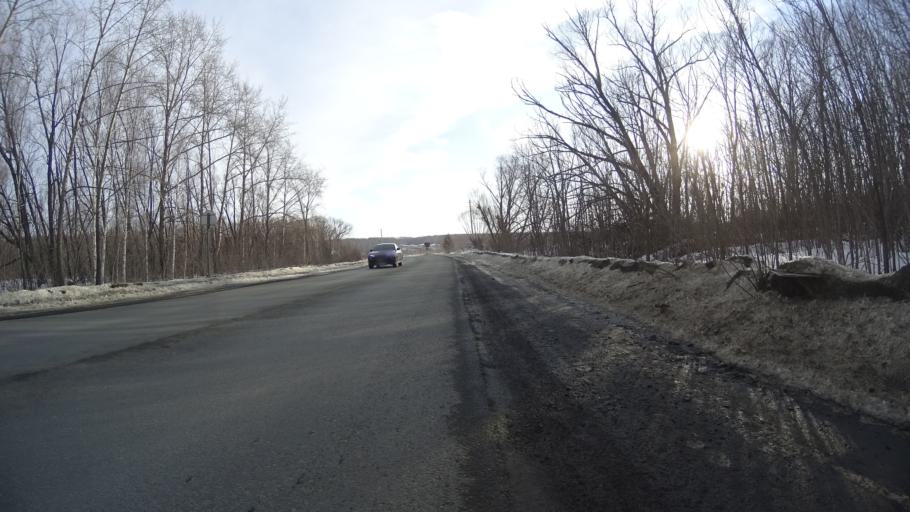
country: RU
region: Chelyabinsk
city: Sargazy
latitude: 55.1413
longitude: 61.2823
